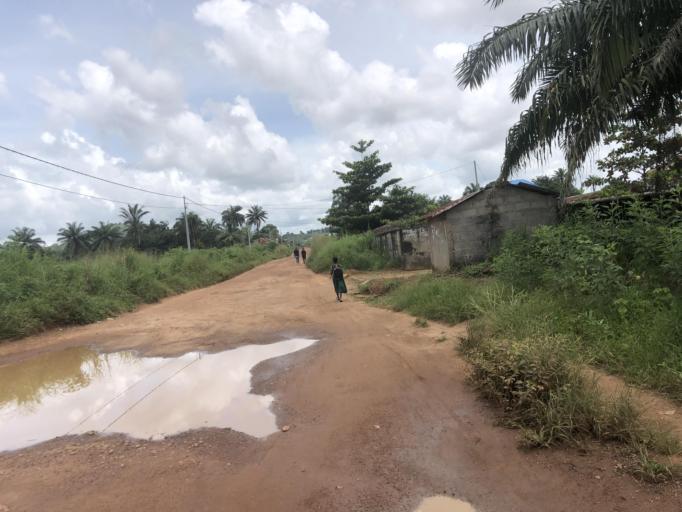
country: SL
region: Northern Province
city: Makeni
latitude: 8.8585
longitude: -12.0554
